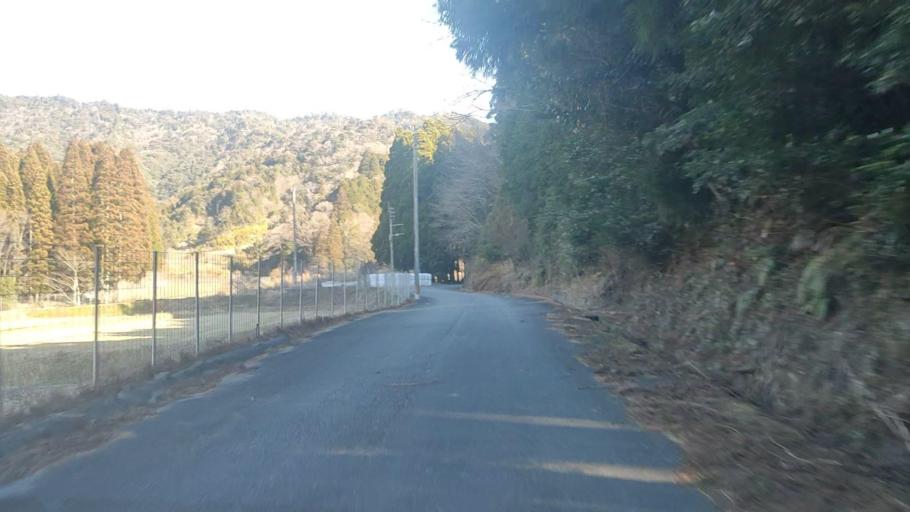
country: JP
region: Oita
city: Saiki
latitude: 32.7801
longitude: 131.8335
